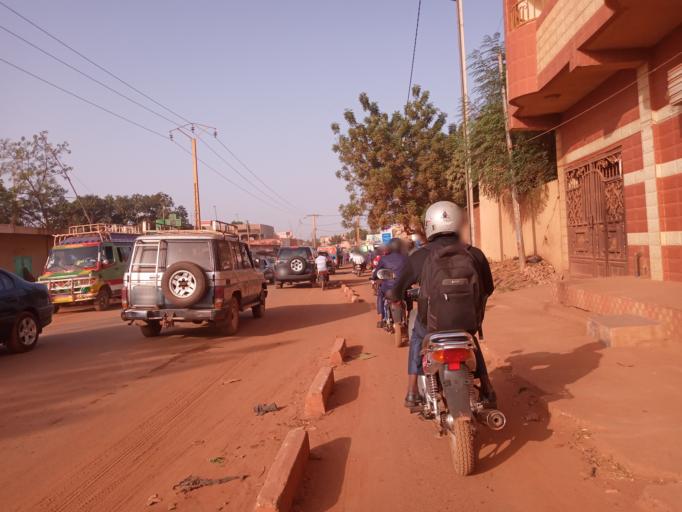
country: ML
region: Bamako
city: Bamako
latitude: 12.5808
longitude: -8.0244
